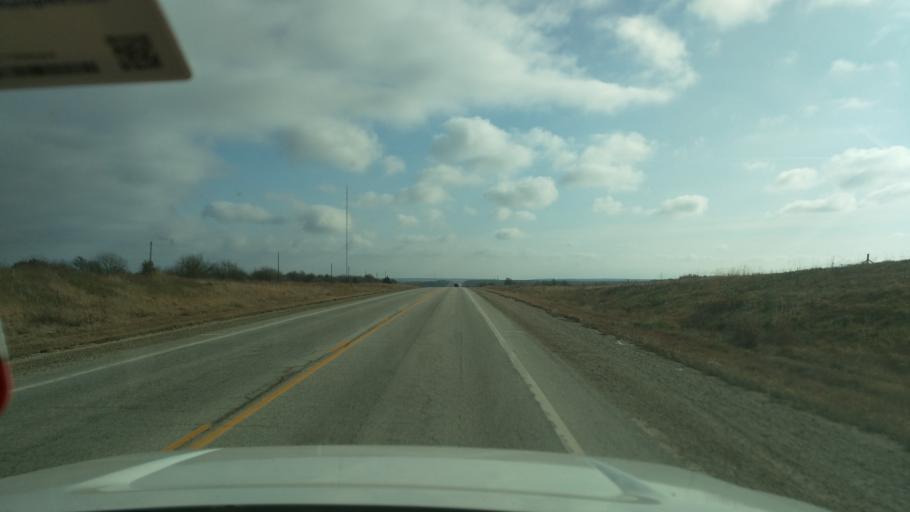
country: US
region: Kansas
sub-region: Chautauqua County
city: Sedan
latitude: 37.0834
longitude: -96.1959
